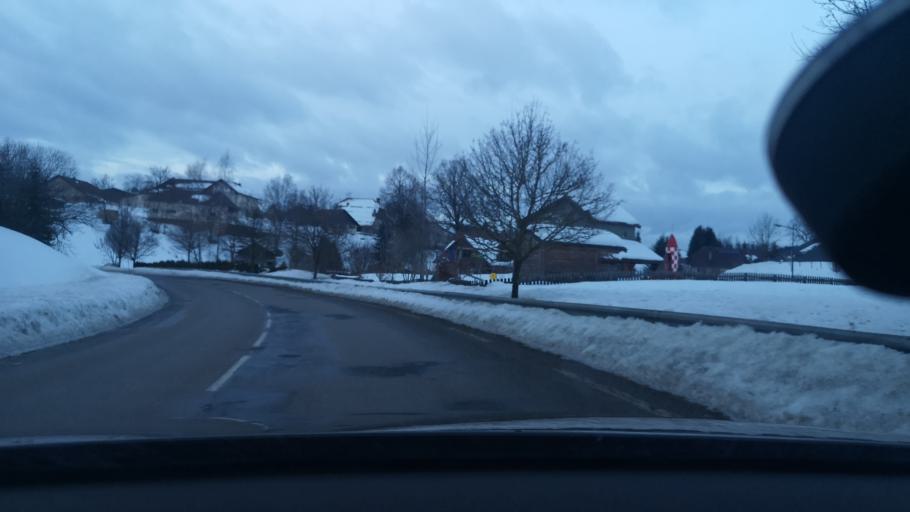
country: FR
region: Franche-Comte
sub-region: Departement du Doubs
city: Jougne
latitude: 46.7887
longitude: 6.3722
